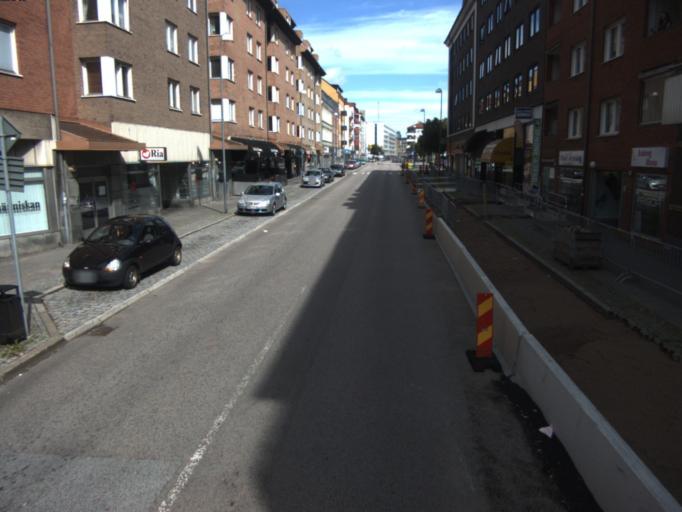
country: SE
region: Skane
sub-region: Helsingborg
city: Helsingborg
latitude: 56.0370
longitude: 12.7028
